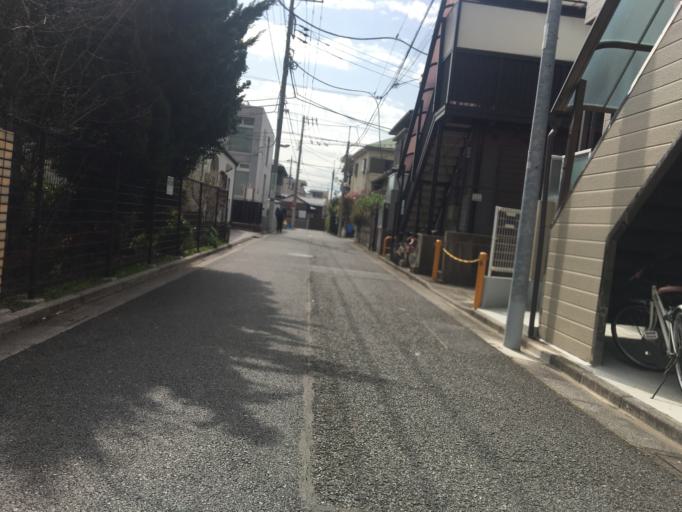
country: JP
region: Tokyo
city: Tokyo
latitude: 35.7413
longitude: 139.6753
